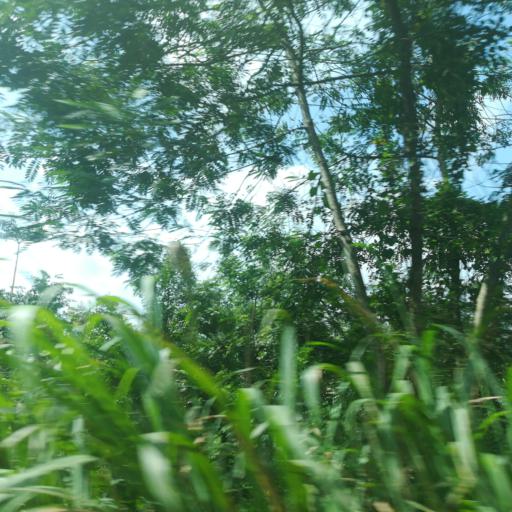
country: NG
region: Lagos
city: Ikorodu
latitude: 6.6743
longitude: 3.6531
